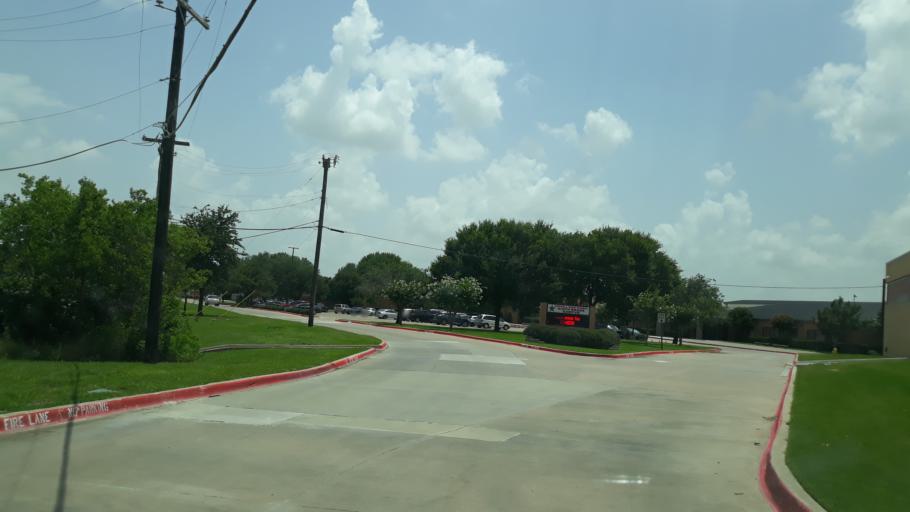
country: US
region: Texas
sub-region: Dallas County
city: Coppell
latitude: 32.9387
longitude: -97.0015
